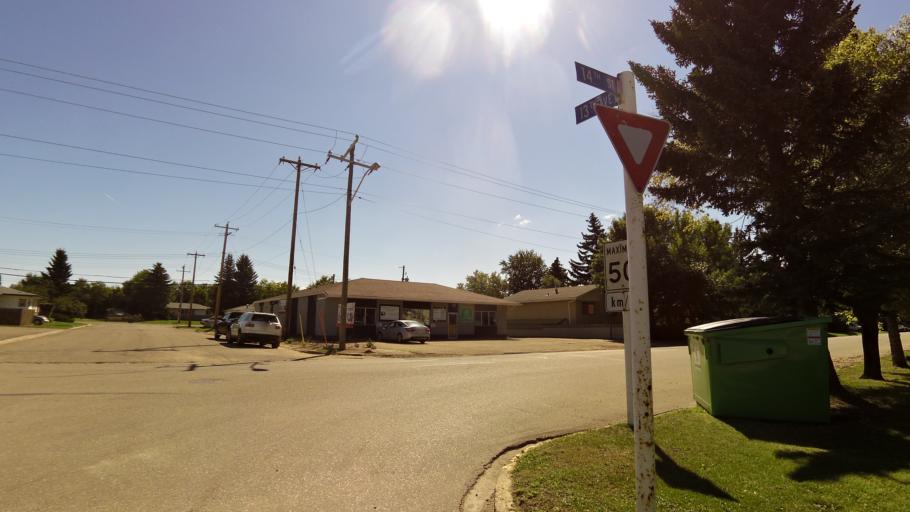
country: CA
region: Alberta
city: Wainwright
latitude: 52.8423
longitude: -110.8507
